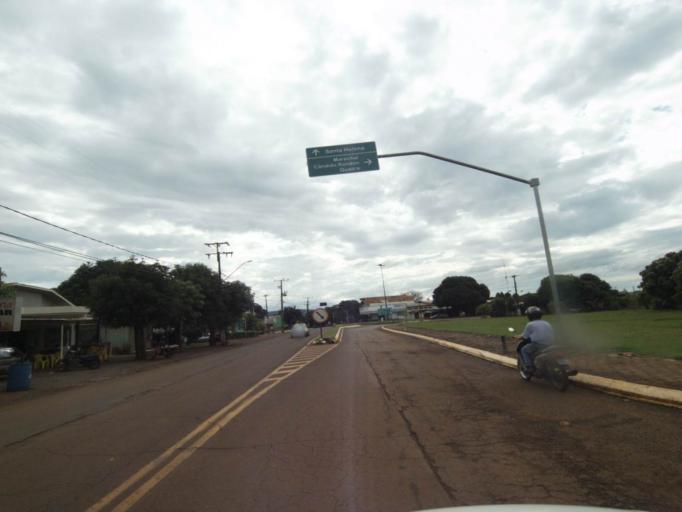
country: BR
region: Parana
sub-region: Marechal Candido Rondon
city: Marechal Candido Rondon
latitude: -24.7823
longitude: -54.2352
